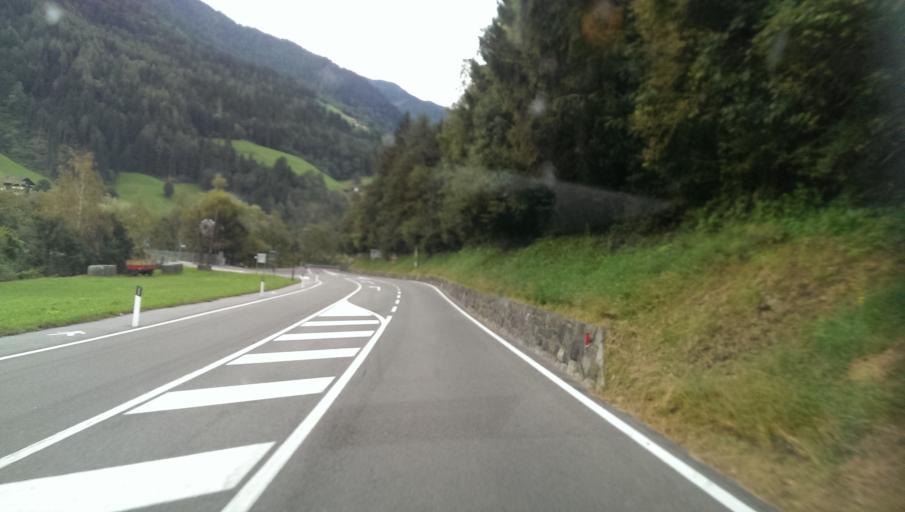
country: IT
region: Trentino-Alto Adige
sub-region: Bolzano
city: San Martino in Passiria
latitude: 46.7897
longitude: 11.2306
